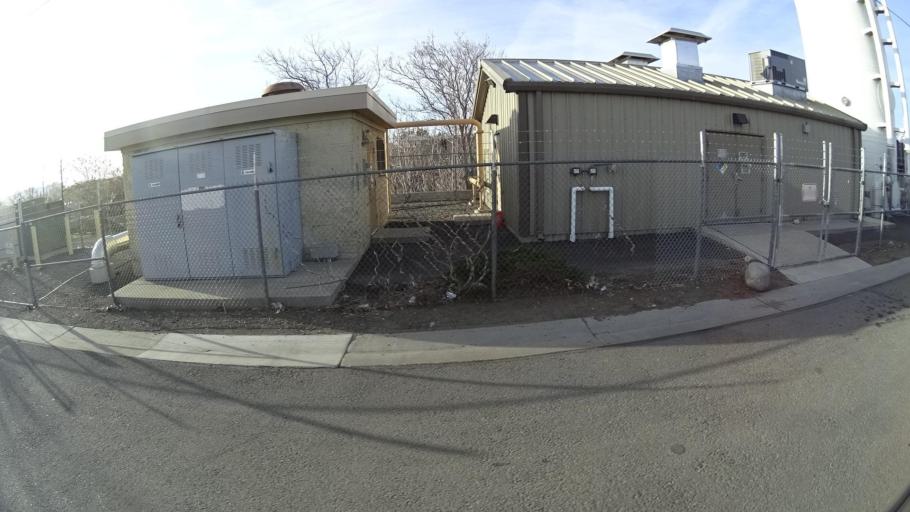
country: US
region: Nevada
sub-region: Washoe County
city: Reno
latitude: 39.5304
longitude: -119.8010
